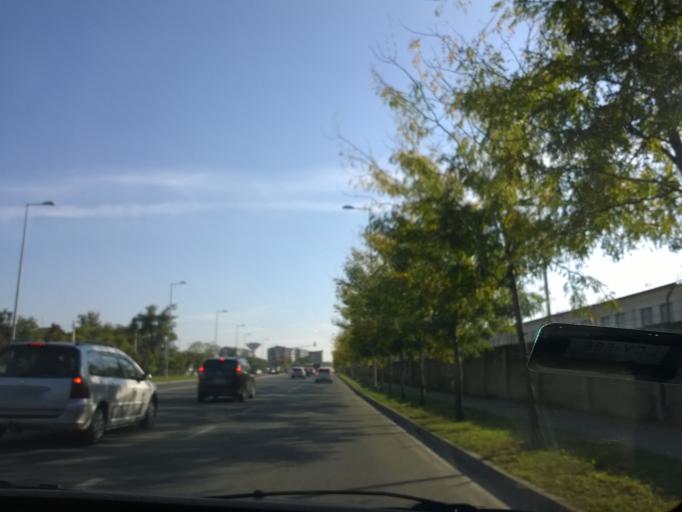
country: HU
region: Budapest
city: Budapest XXI. keruelet
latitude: 47.4334
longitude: 19.0660
